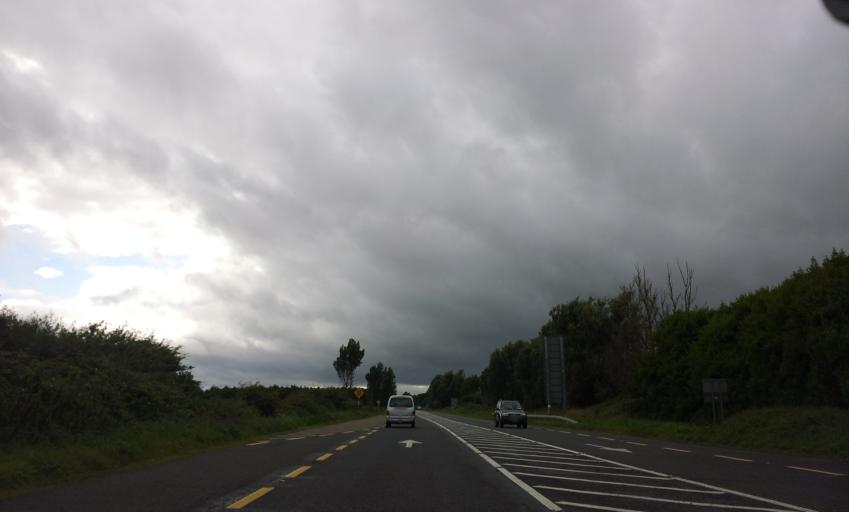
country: IE
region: Munster
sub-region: County Cork
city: Youghal
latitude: 51.9392
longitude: -7.9085
